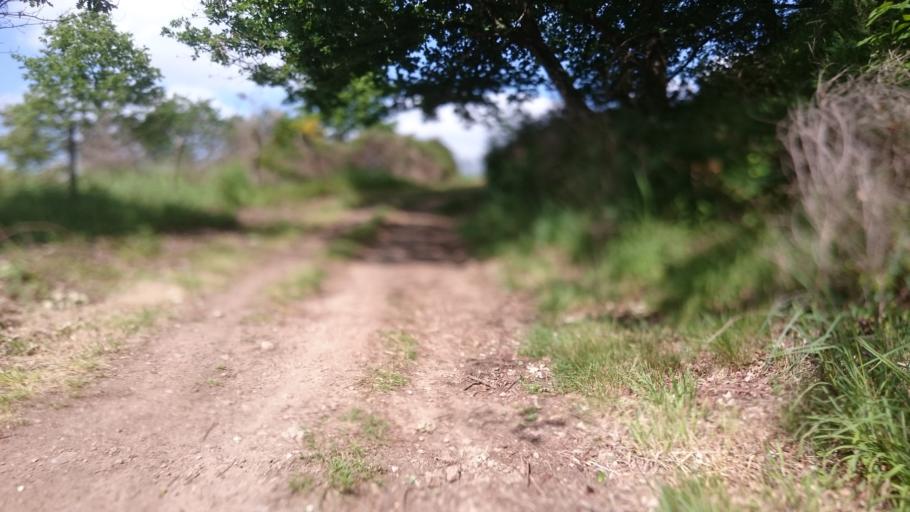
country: FR
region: Pays de la Loire
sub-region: Departement de la Loire-Atlantique
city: Indre
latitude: 47.1829
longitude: -1.6513
